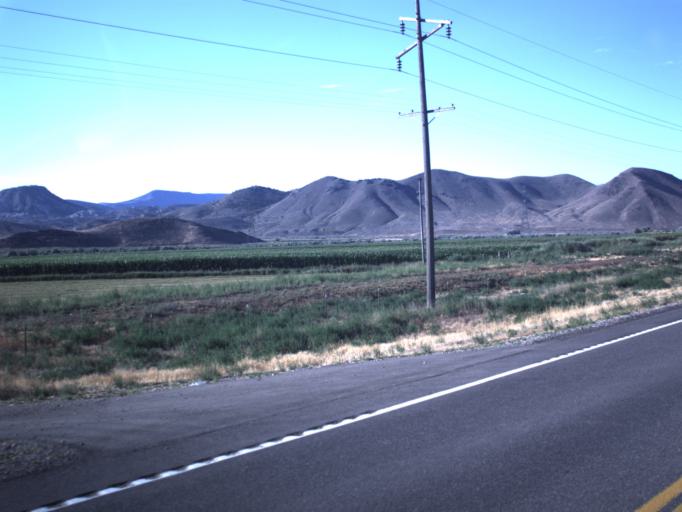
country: US
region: Utah
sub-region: Sevier County
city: Aurora
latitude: 38.9054
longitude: -111.9388
